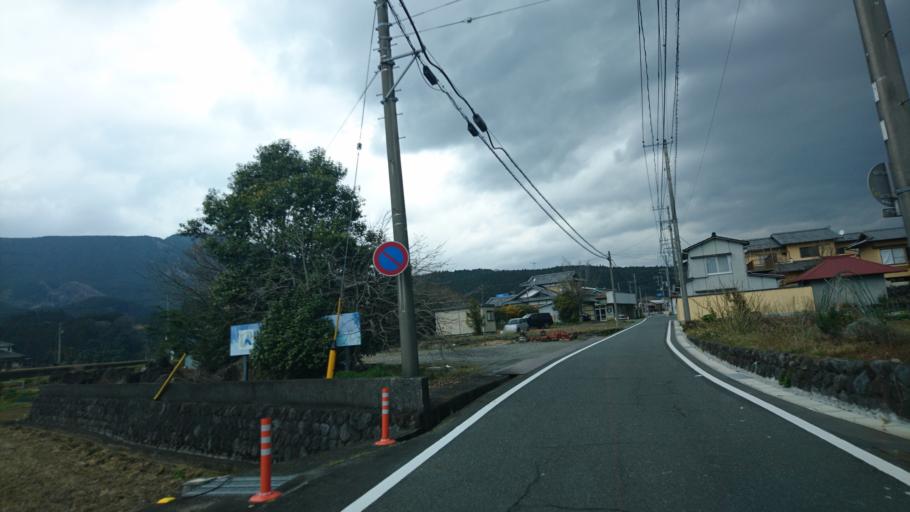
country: JP
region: Shizuoka
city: Fujinomiya
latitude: 35.2843
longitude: 138.5770
